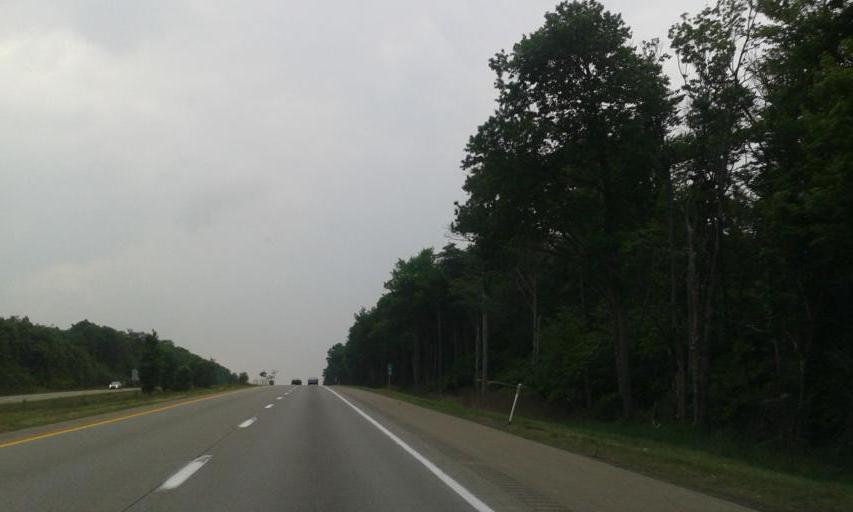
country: US
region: Pennsylvania
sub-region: Monroe County
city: Pocono Pines
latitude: 41.1940
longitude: -75.4469
